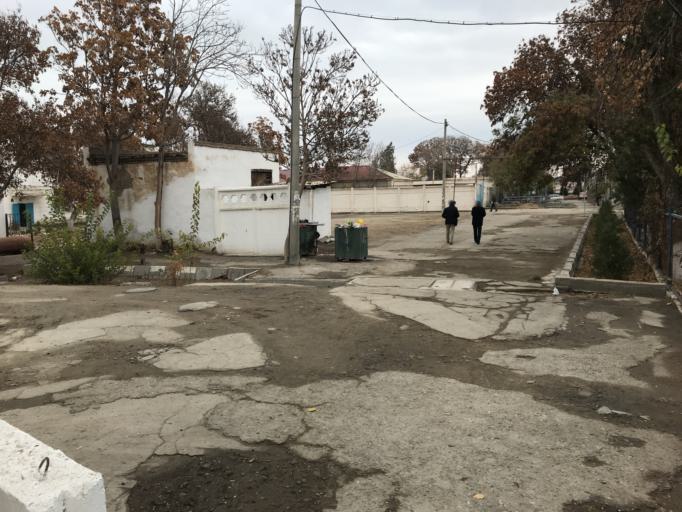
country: UZ
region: Bukhara
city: Kogon
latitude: 39.7223
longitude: 64.5460
